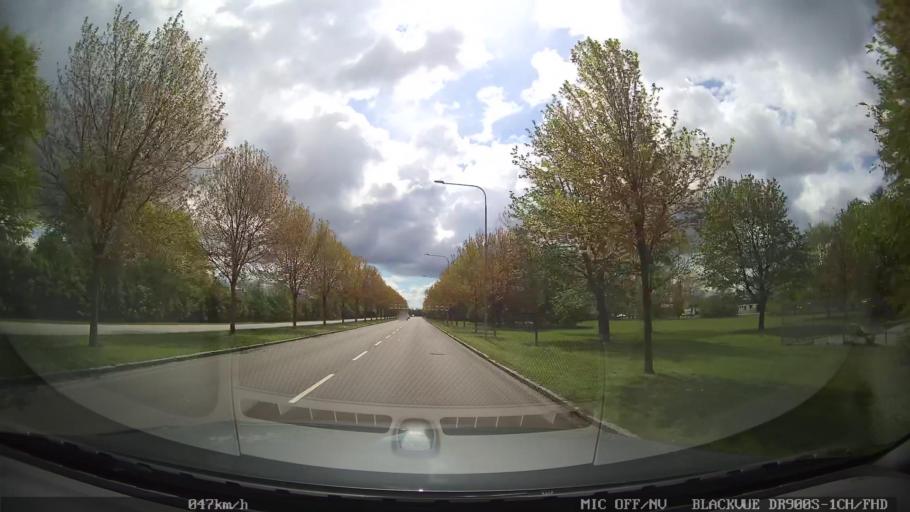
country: SE
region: Skane
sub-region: Landskrona
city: Landskrona
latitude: 55.8947
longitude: 12.8149
